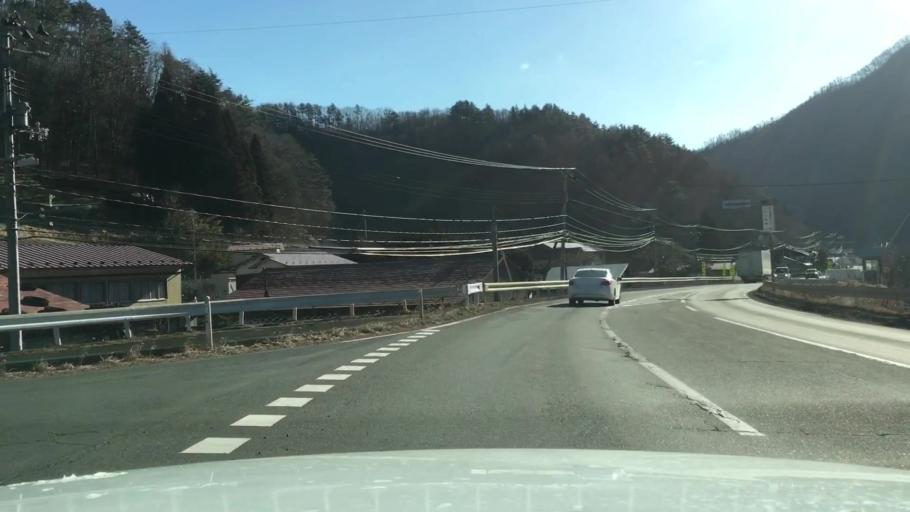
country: JP
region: Iwate
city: Tono
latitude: 39.6150
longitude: 141.6272
